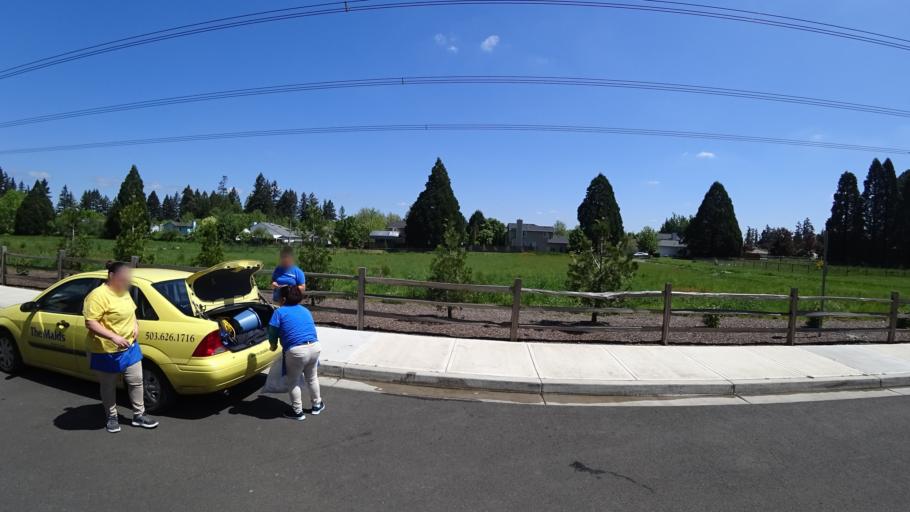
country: US
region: Oregon
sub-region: Washington County
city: Aloha
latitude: 45.5171
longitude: -122.8974
